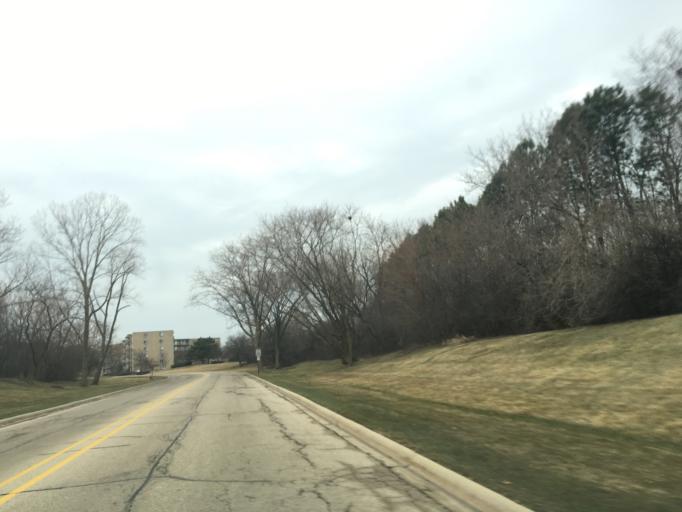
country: US
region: Illinois
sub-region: Cook County
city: Hoffman Estates
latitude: 42.0555
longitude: -88.0831
